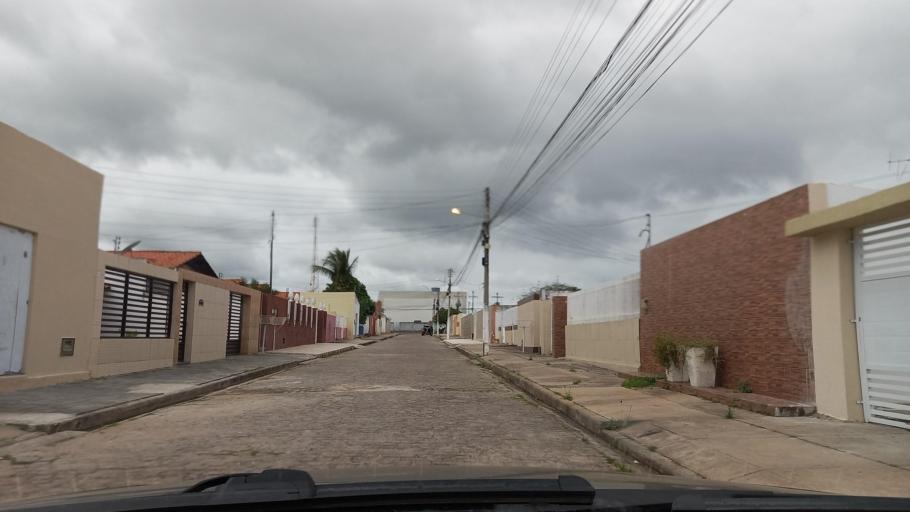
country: BR
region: Sergipe
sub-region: Caninde De Sao Francisco
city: Caninde de Sao Francisco
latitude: -9.6095
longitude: -37.7649
